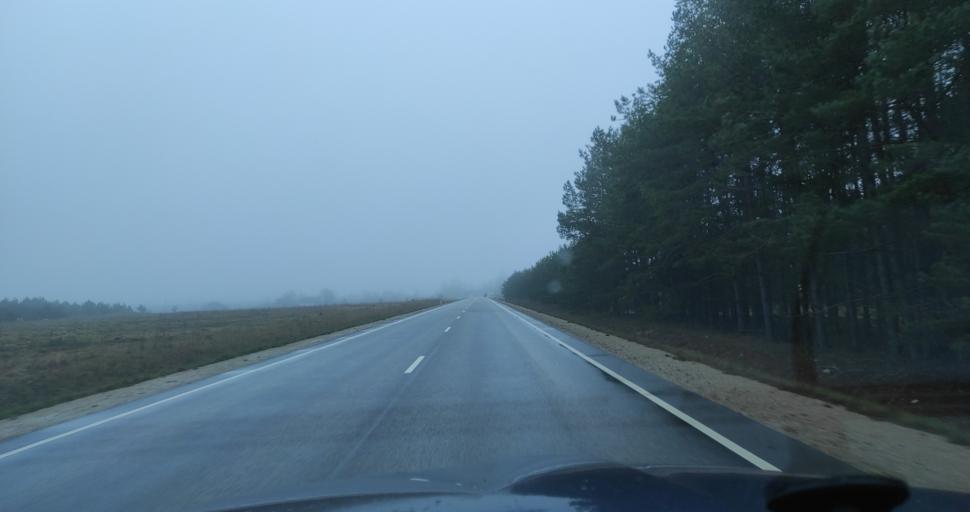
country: LV
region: Pavilostas
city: Pavilosta
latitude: 56.9405
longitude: 21.2823
